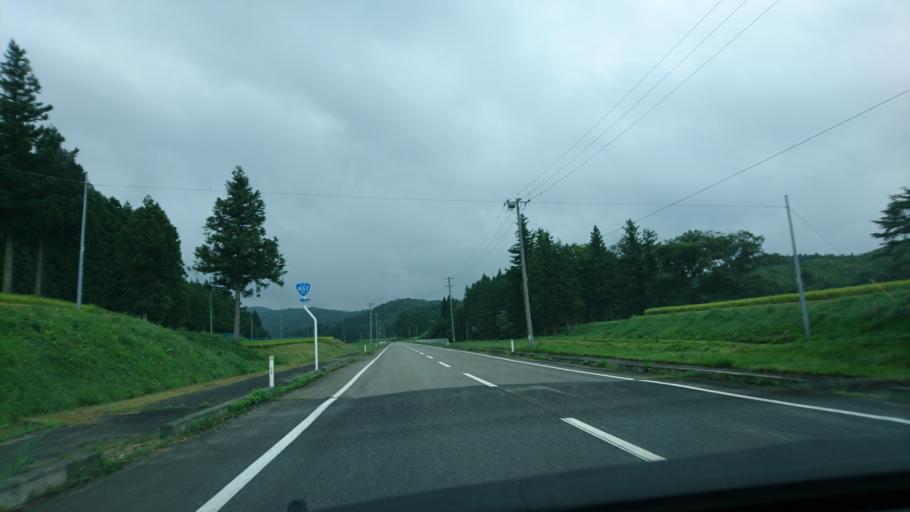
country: JP
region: Iwate
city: Ichinoseki
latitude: 38.8868
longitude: 140.9619
